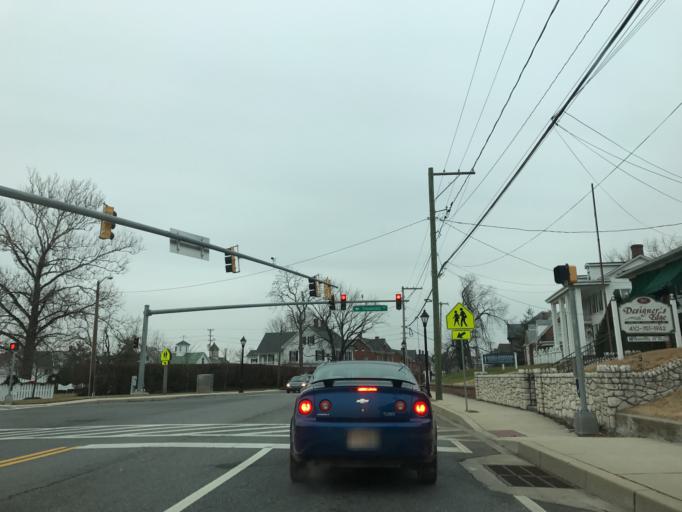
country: US
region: Maryland
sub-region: Carroll County
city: Taneytown
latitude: 39.6564
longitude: -77.1722
